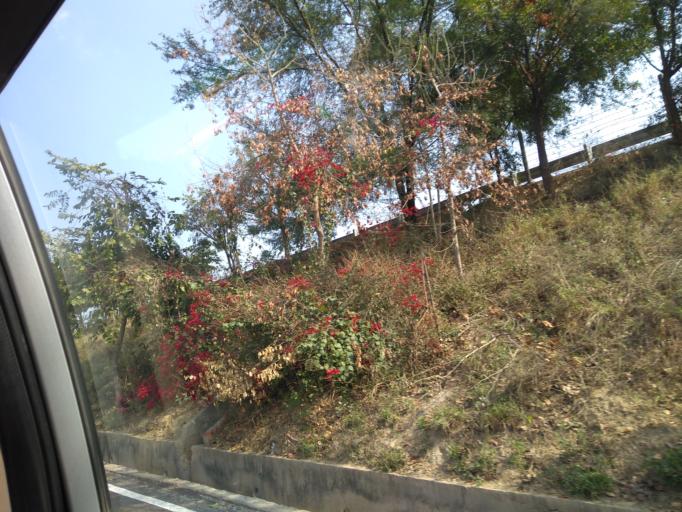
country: IN
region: Uttar Pradesh
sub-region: Mathura
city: Vrindavan
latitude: 27.6125
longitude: 77.7425
